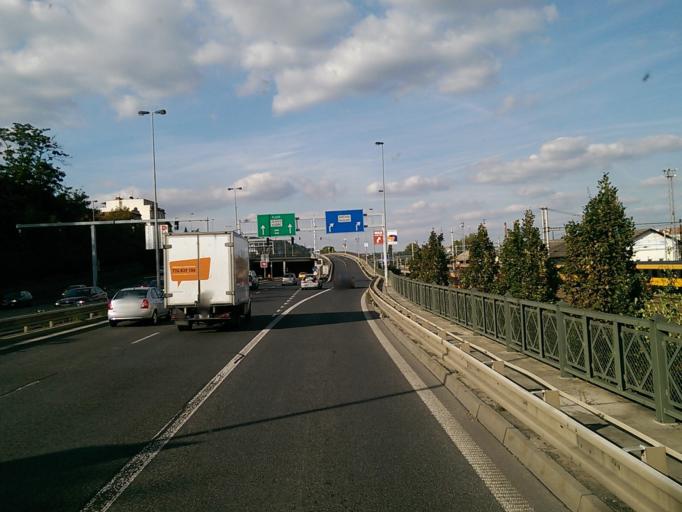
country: CZ
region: Praha
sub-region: Praha 2
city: Vysehrad
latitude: 50.0599
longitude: 14.4065
